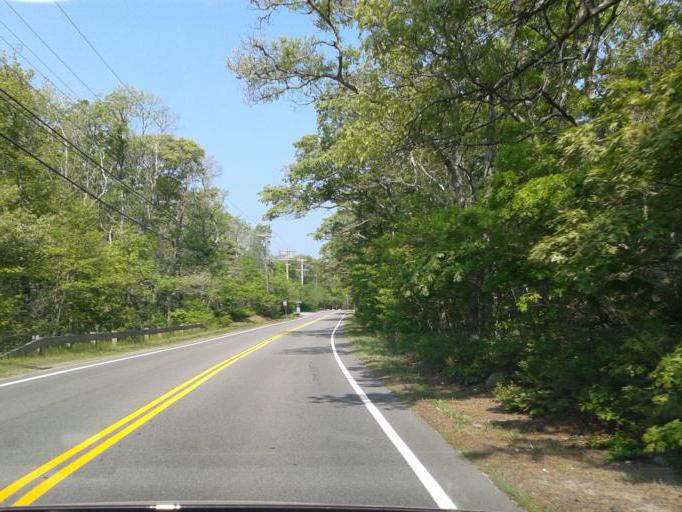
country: US
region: Massachusetts
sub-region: Barnstable County
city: West Falmouth
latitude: 41.6147
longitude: -70.6127
